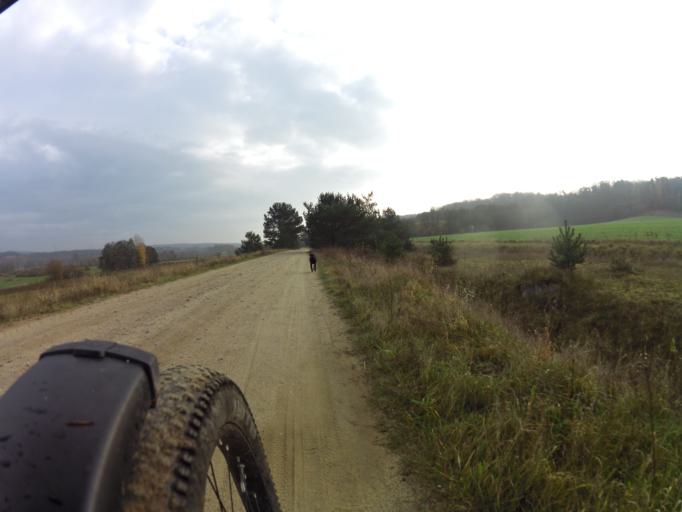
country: PL
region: Pomeranian Voivodeship
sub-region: Powiat wejherowski
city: Gniewino
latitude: 54.7062
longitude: 18.1028
